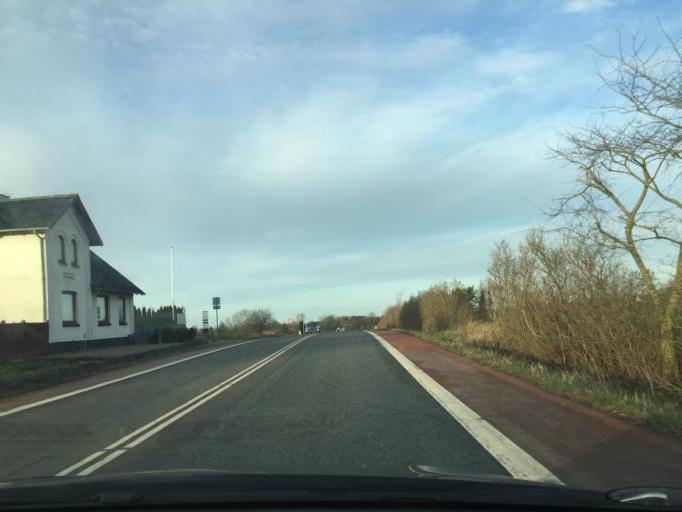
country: DK
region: South Denmark
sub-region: Faaborg-Midtfyn Kommune
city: Arslev
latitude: 55.2730
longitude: 10.4506
